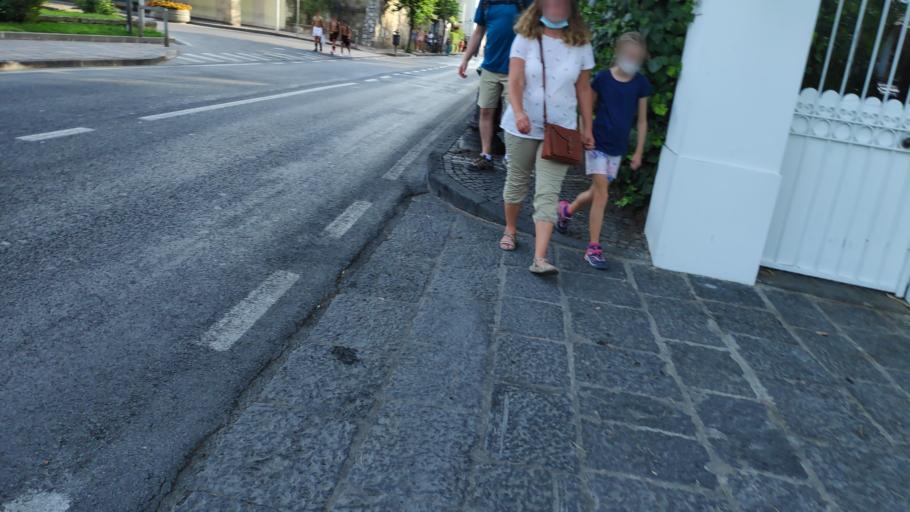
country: IT
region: Campania
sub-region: Provincia di Napoli
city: Sorrento
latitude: 40.6281
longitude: 14.3783
